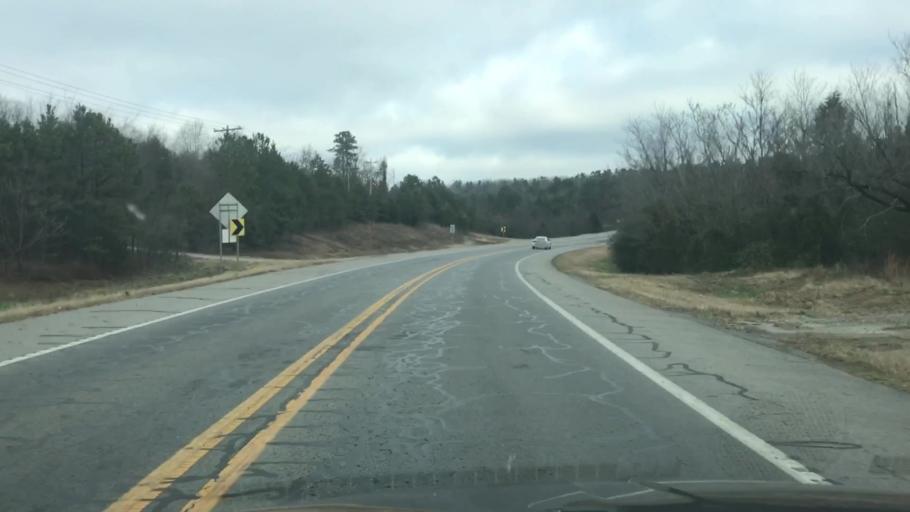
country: US
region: Arkansas
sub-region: Scott County
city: Waldron
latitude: 34.8106
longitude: -94.0400
